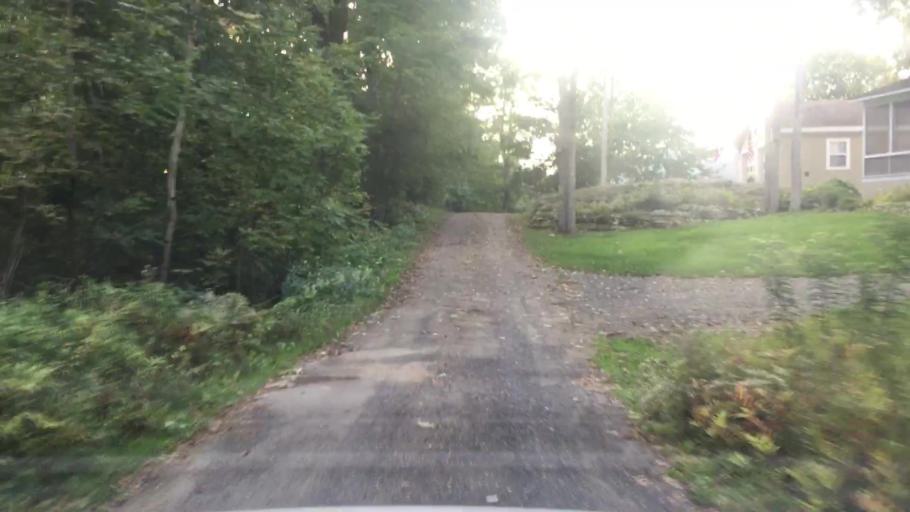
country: US
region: Maine
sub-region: Lincoln County
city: Boothbay
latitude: 43.9077
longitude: -69.6580
